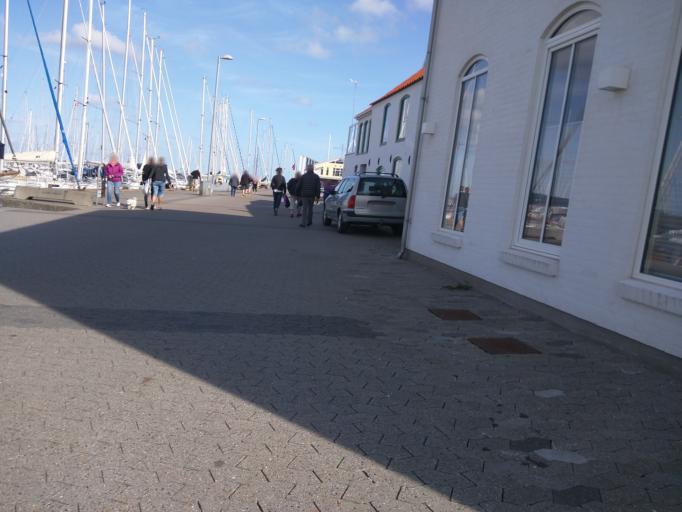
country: DK
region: North Denmark
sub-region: Frederikshavn Kommune
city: Saeby
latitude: 57.3336
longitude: 10.5297
